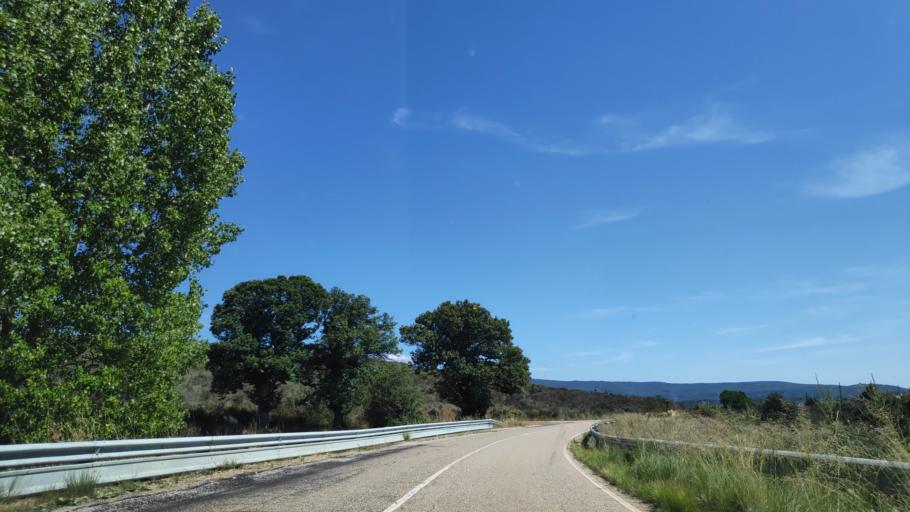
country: ES
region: Castille and Leon
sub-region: Provincia de Zamora
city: Puebla de Sanabria
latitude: 42.0481
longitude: -6.6458
